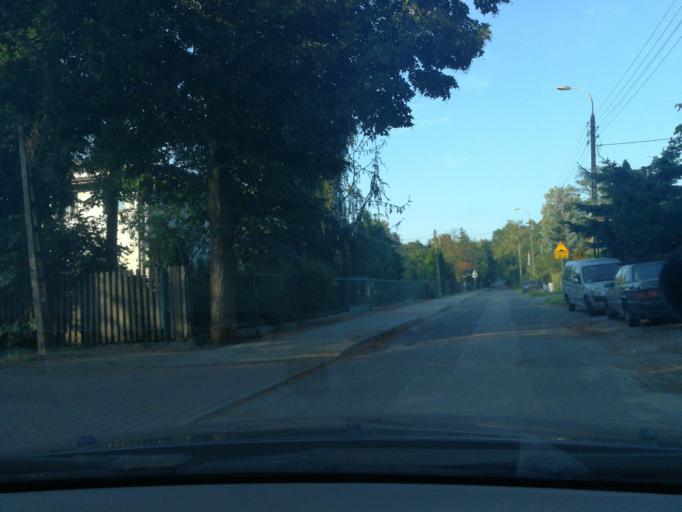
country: PL
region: Masovian Voivodeship
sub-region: Powiat pruszkowski
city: Brwinow
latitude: 52.1354
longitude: 20.7131
